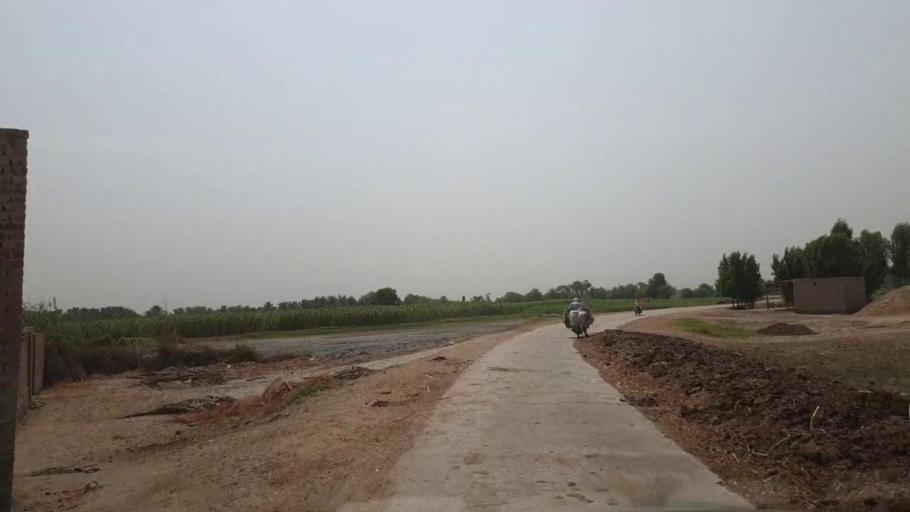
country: PK
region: Sindh
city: Gambat
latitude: 27.4446
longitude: 68.5147
